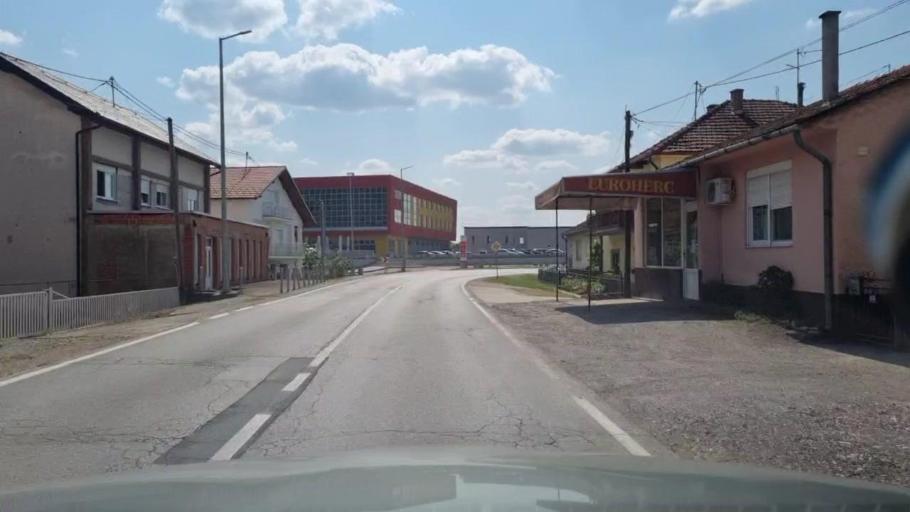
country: BA
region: Republika Srpska
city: Ostra Luka
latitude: 45.0630
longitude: 18.5821
